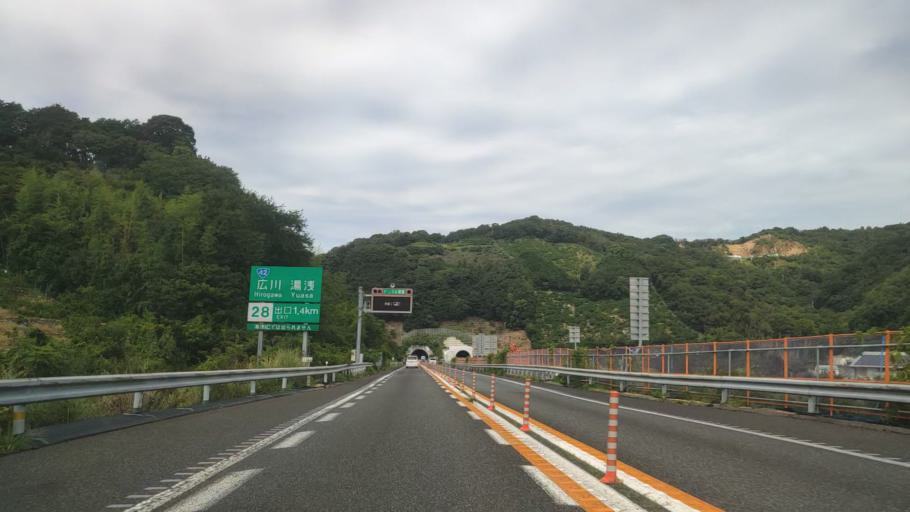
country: JP
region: Wakayama
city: Gobo
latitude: 33.9955
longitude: 135.1975
